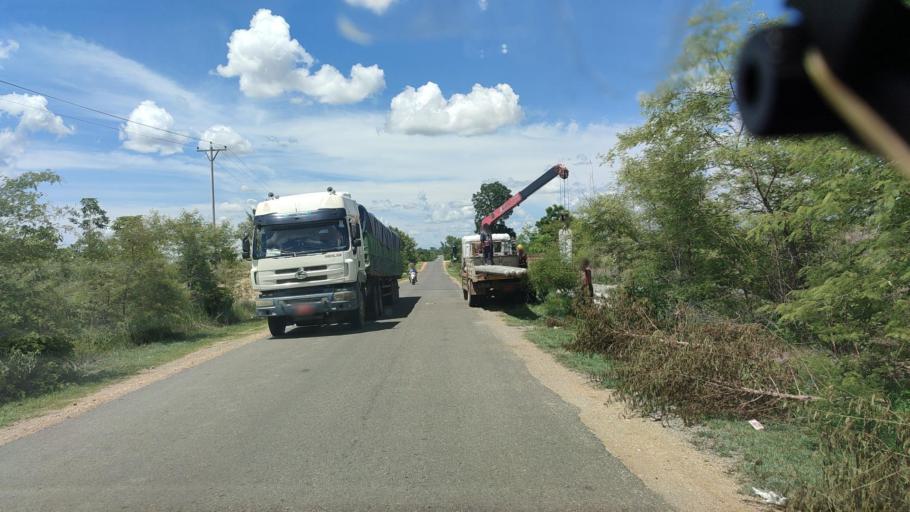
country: MM
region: Magway
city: Taungdwingyi
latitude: 19.7142
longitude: 95.3891
